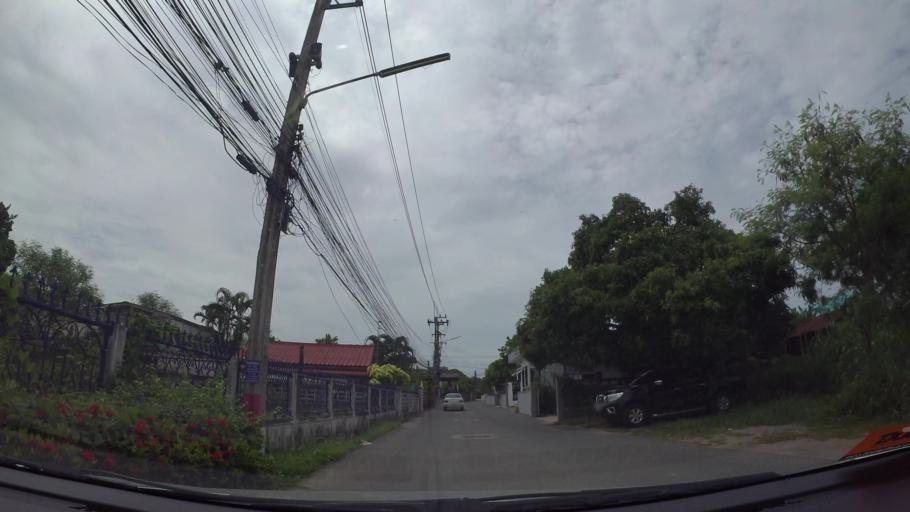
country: TH
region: Chon Buri
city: Sattahip
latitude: 12.6800
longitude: 100.8961
